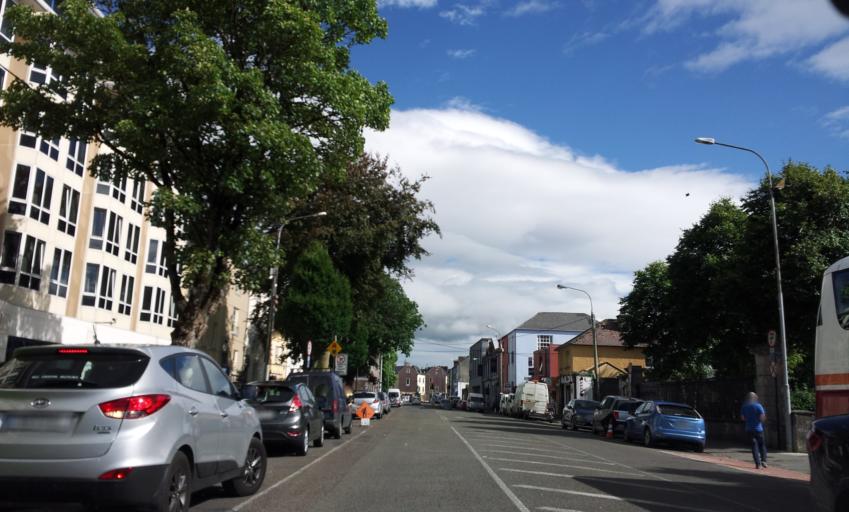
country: IE
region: Munster
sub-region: Ciarrai
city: Tralee
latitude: 52.2668
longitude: -9.7100
